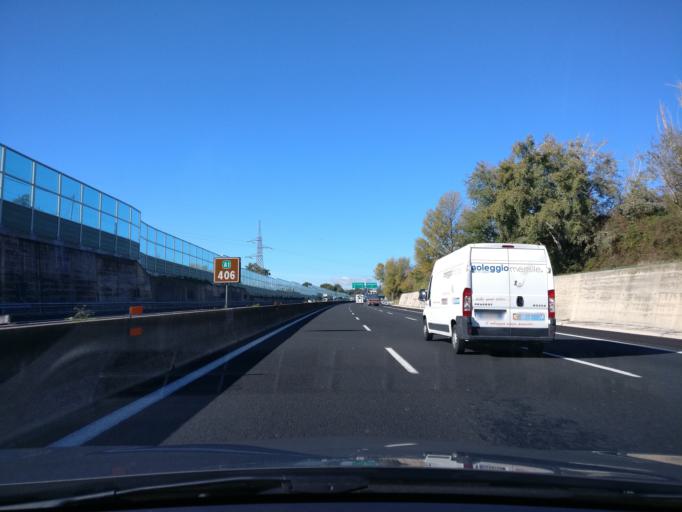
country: IT
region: Latium
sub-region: Provincia di Frosinone
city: Ceprano
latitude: 41.5427
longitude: 13.5035
